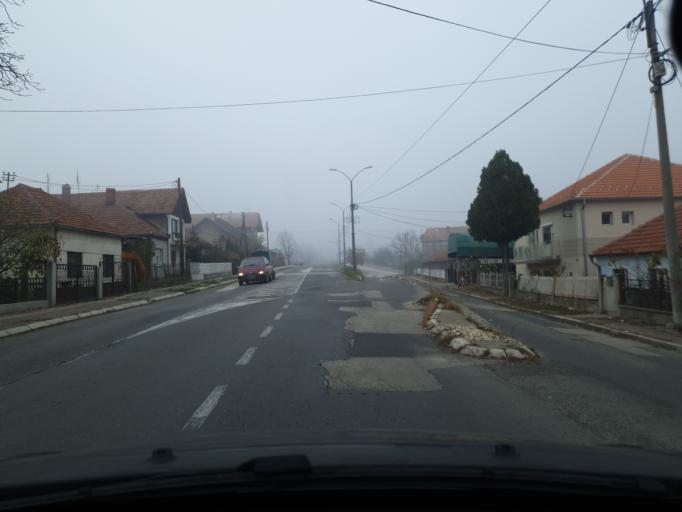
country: RS
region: Central Serbia
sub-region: Zajecarski Okrug
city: Zajecar
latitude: 43.8977
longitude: 22.2622
